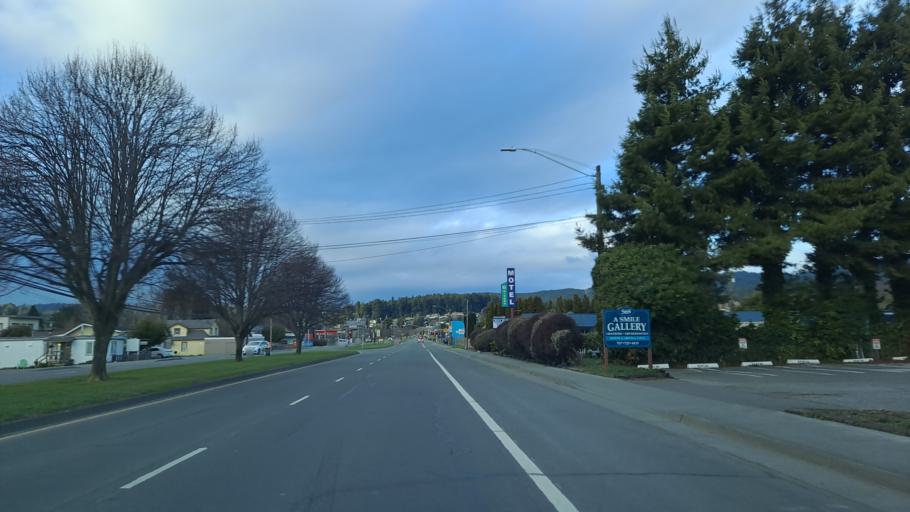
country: US
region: California
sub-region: Humboldt County
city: Fortuna
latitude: 40.5862
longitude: -124.1467
